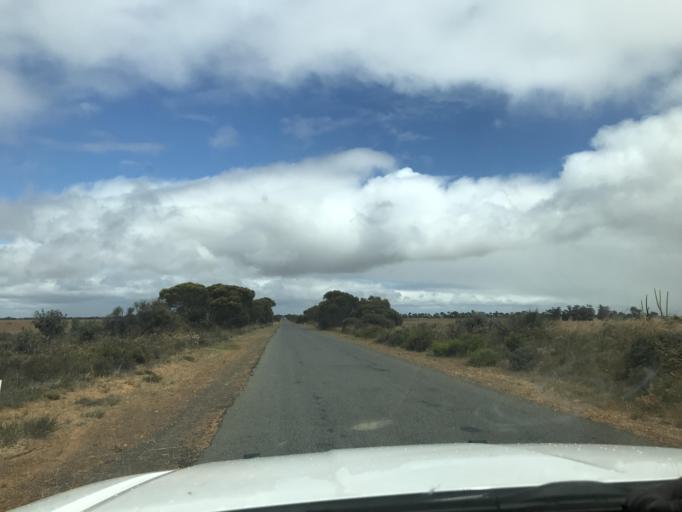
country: AU
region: South Australia
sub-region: Tatiara
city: Bordertown
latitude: -36.1389
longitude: 141.2137
